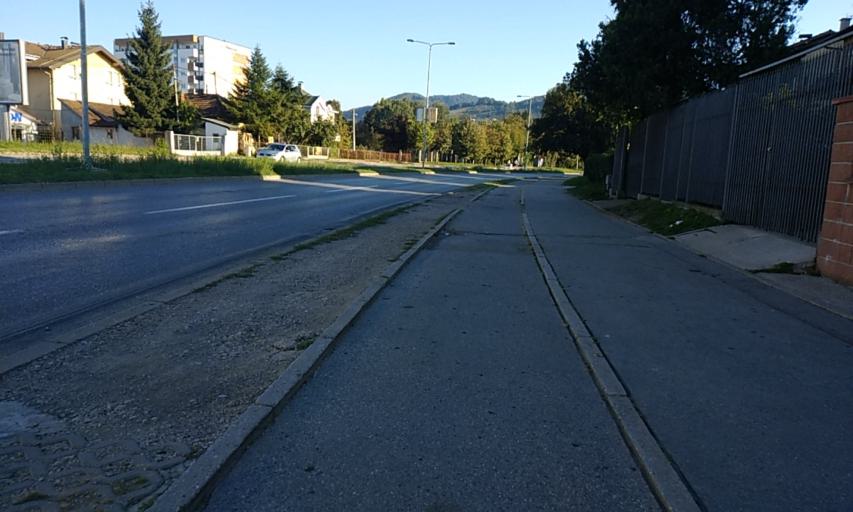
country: BA
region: Republika Srpska
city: Starcevica
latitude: 44.7698
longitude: 17.2100
